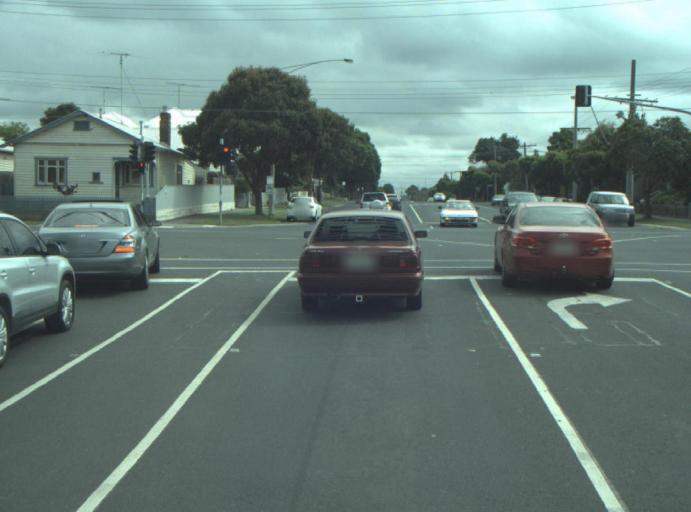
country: AU
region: Victoria
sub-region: Greater Geelong
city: Geelong
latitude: -38.1627
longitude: 144.3565
